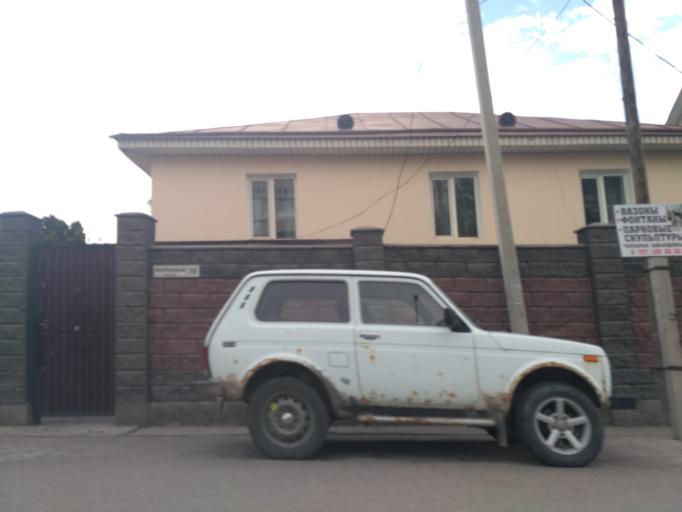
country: KZ
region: Almaty Oblysy
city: Burunday
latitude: 43.2057
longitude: 76.6368
